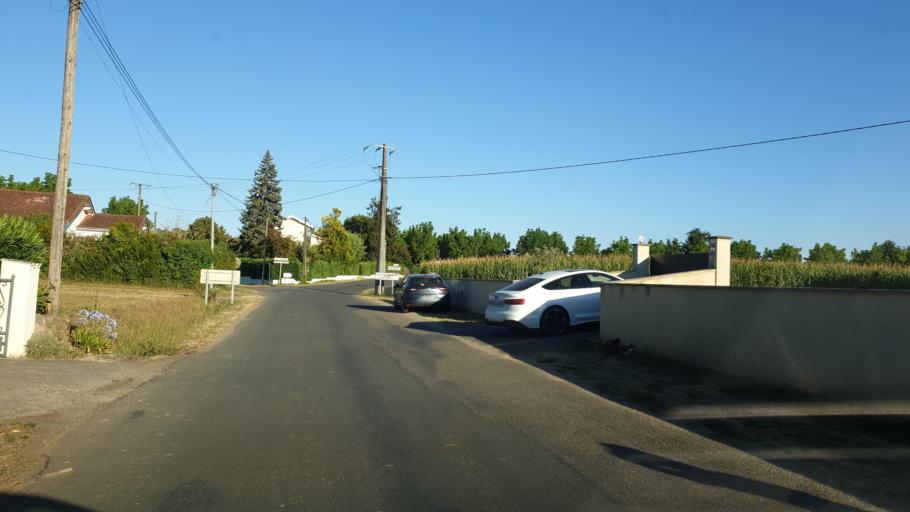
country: FR
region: Aquitaine
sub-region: Departement du Lot-et-Garonne
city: Castelmoron-sur-Lot
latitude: 44.3921
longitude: 0.5036
